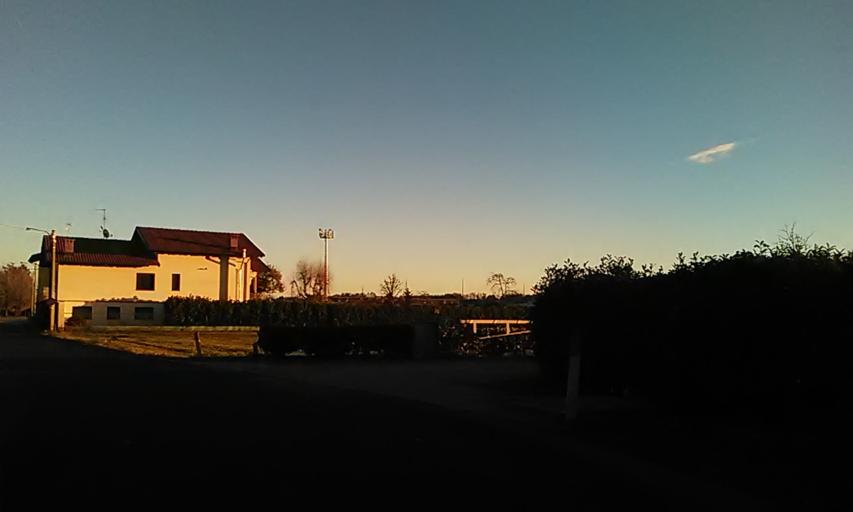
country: IT
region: Piedmont
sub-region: Provincia di Biella
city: Ronco Biellese
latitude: 45.5630
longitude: 8.0780
